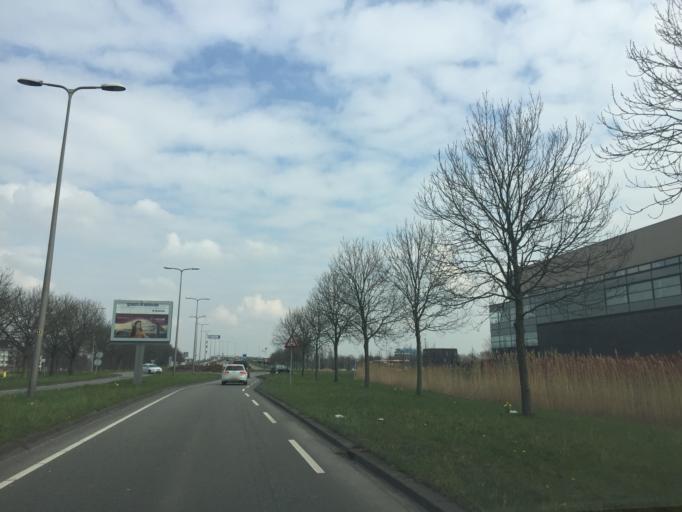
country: NL
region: South Holland
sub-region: Gemeente Alphen aan den Rijn
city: Alphen aan den Rijn
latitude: 52.1138
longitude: 4.6609
